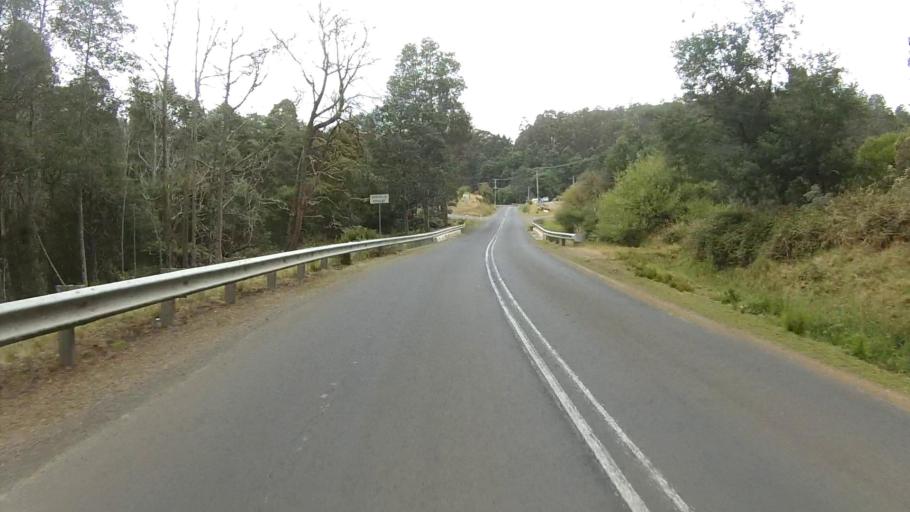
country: AU
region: Tasmania
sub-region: Huon Valley
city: Cygnet
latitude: -43.1435
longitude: 147.1535
